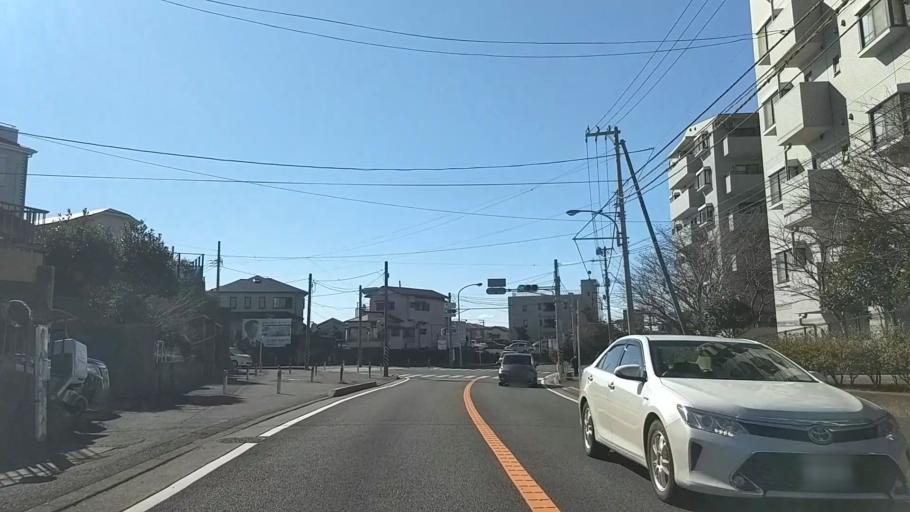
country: JP
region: Kanagawa
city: Yokosuka
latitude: 35.2093
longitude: 139.6850
